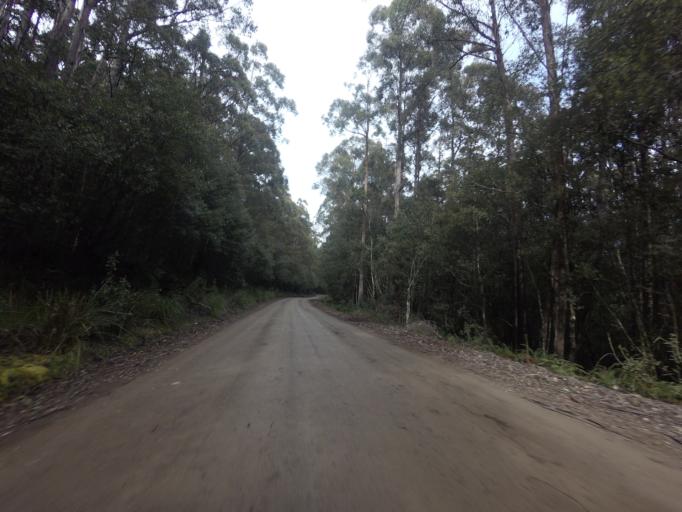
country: AU
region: Tasmania
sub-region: Huon Valley
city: Geeveston
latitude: -43.4935
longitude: 146.8814
